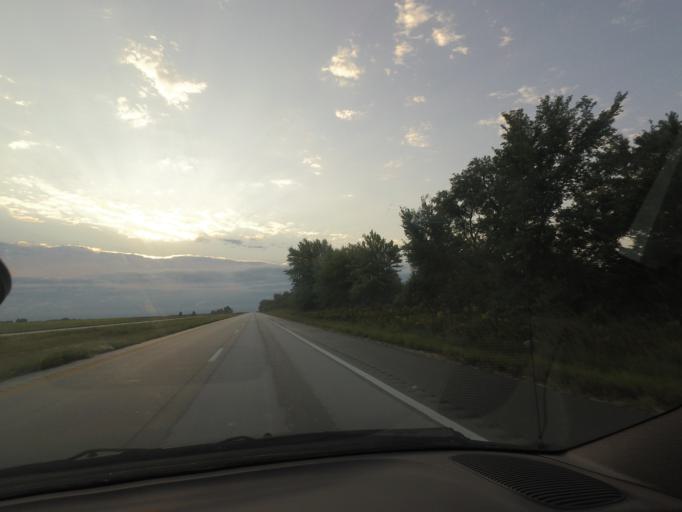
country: US
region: Missouri
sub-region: Shelby County
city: Shelbina
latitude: 39.7297
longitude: -92.1944
